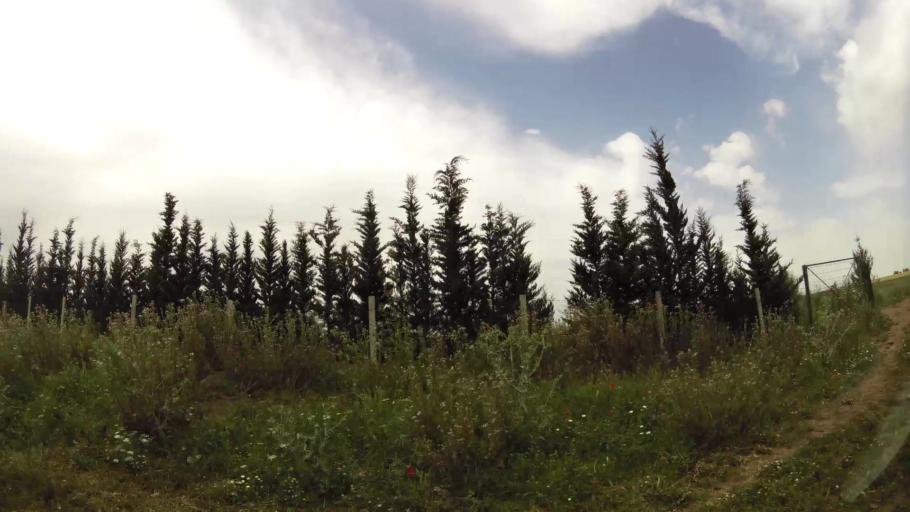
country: MA
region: Rabat-Sale-Zemmour-Zaer
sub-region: Khemisset
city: Tiflet
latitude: 33.7571
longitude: -6.2291
